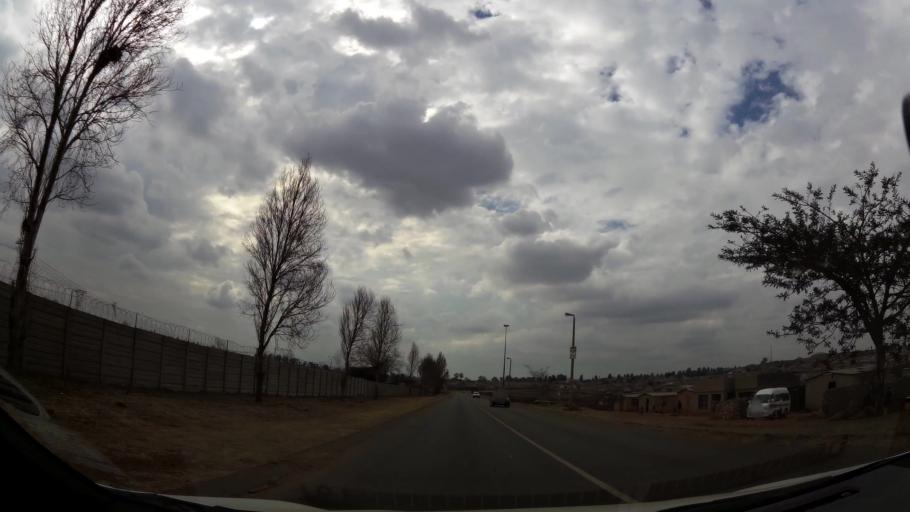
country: ZA
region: Gauteng
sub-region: Ekurhuleni Metropolitan Municipality
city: Germiston
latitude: -26.3786
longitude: 28.1132
